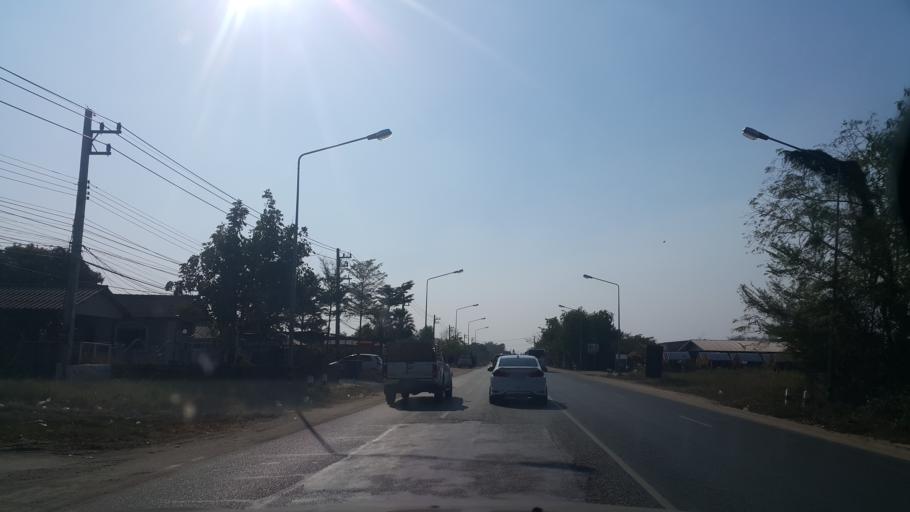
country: TH
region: Nakhon Ratchasima
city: Phimai
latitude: 15.2144
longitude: 102.4826
